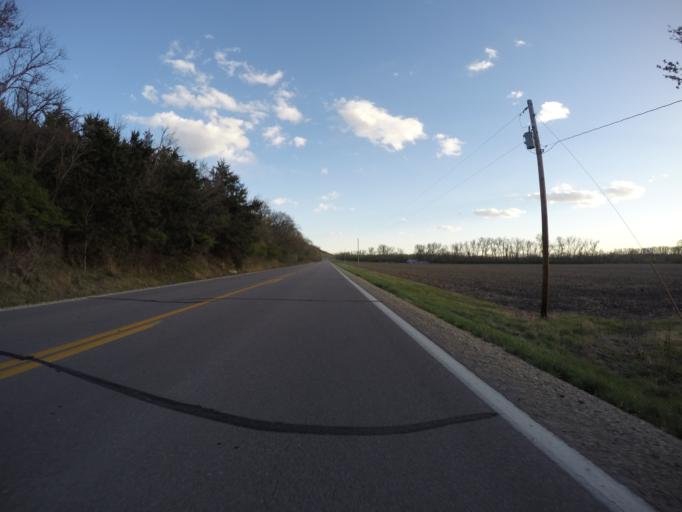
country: US
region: Kansas
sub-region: Riley County
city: Manhattan
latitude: 39.1519
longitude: -96.5578
